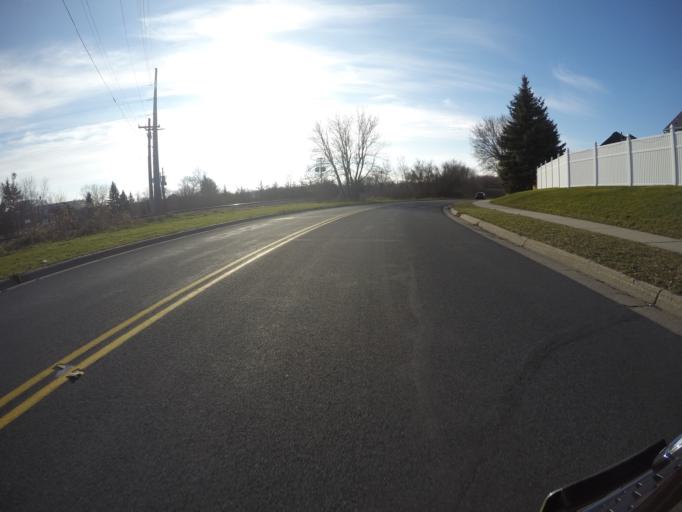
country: US
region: Minnesota
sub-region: Hennepin County
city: Eden Prairie
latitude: 44.8740
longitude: -93.4957
